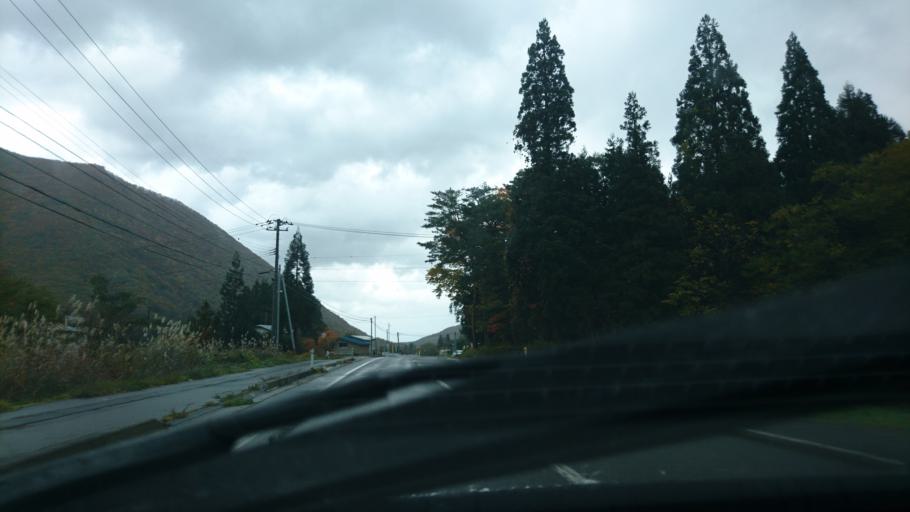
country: JP
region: Iwate
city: Shizukuishi
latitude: 39.6006
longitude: 140.9267
